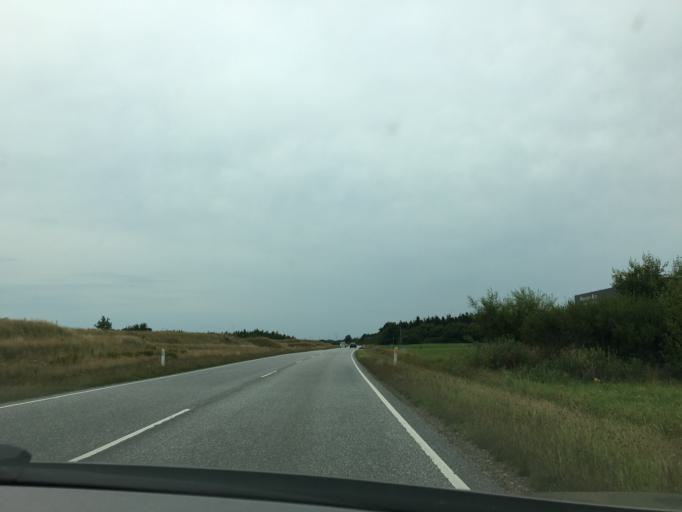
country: DK
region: Central Jutland
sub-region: Ringkobing-Skjern Kommune
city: Ringkobing
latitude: 56.0934
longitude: 8.2774
